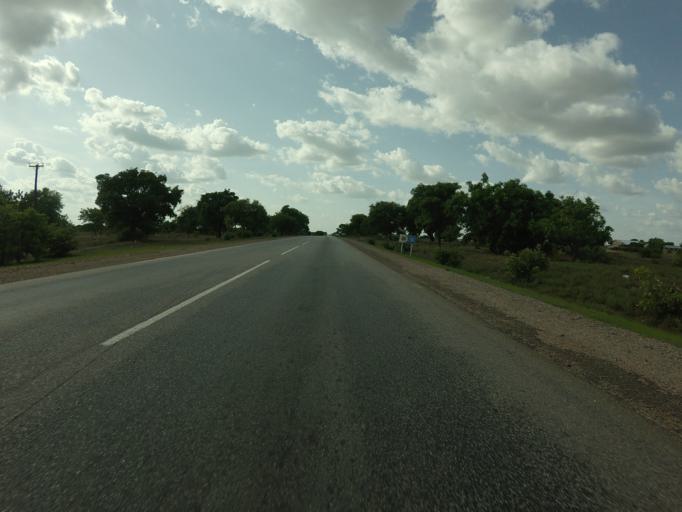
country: GH
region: Upper East
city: Bolgatanga
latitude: 10.6632
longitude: -0.8597
